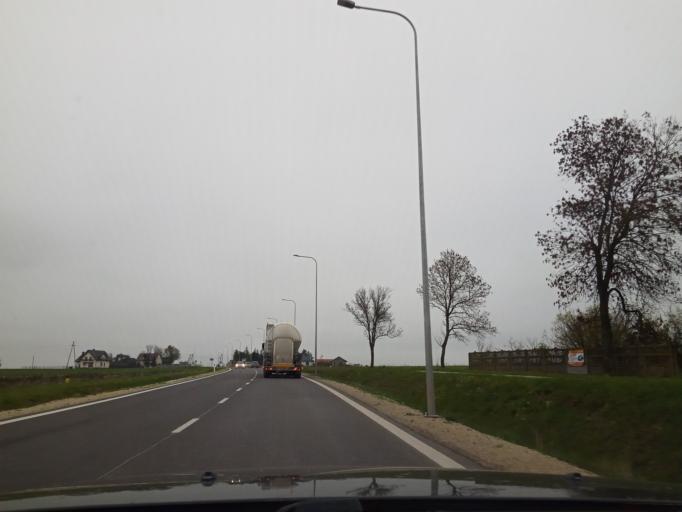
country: PL
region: Swietokrzyskie
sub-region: Powiat jedrzejowski
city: Jedrzejow
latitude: 50.5950
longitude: 20.3227
